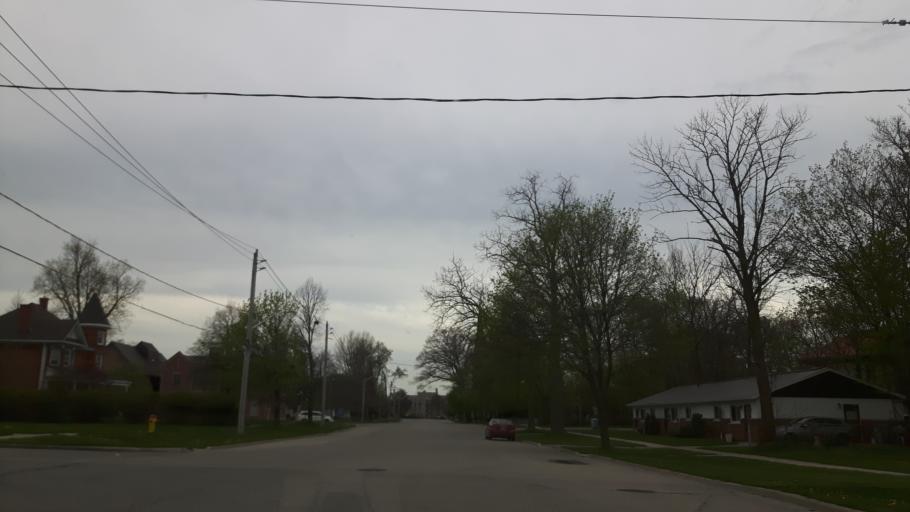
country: CA
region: Ontario
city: Goderich
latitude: 43.7481
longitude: -81.7113
